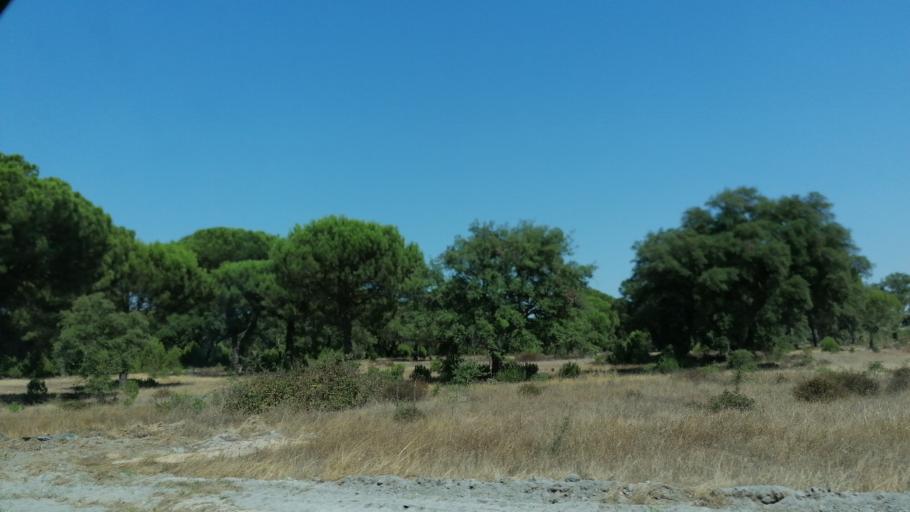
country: PT
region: Santarem
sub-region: Benavente
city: Poceirao
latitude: 38.7343
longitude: -8.6996
